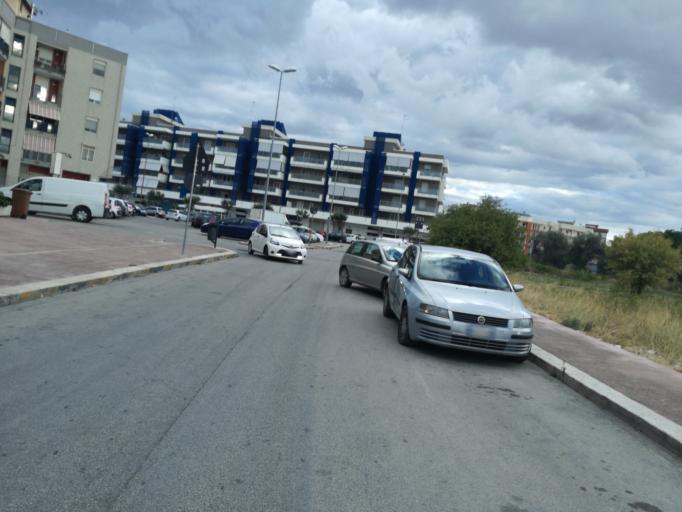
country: IT
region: Apulia
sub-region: Provincia di Bari
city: Triggiano
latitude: 41.0694
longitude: 16.9306
